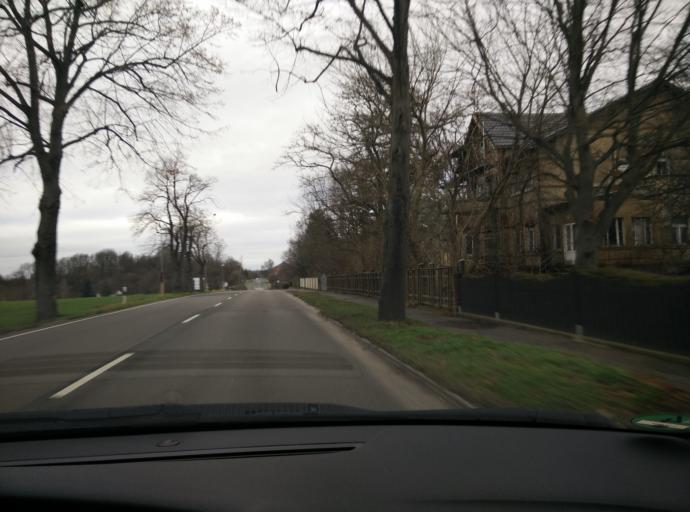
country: DE
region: Saxony
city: Frohburg
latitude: 51.0867
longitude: 12.5303
